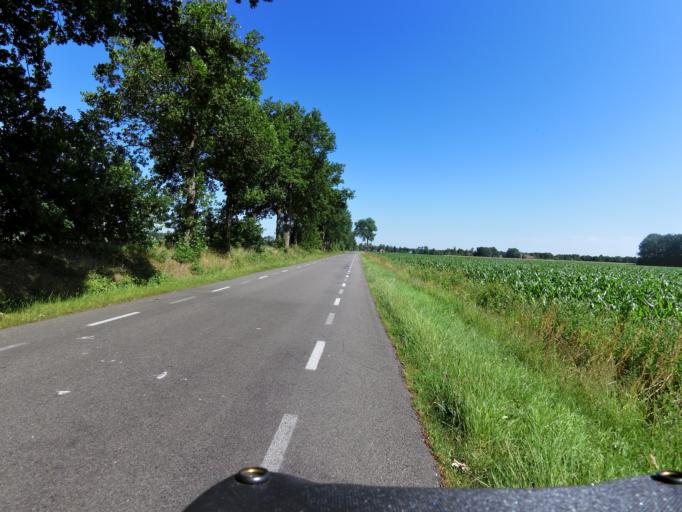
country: NL
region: Overijssel
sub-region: Gemeente Twenterand
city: Den Ham
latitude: 52.5311
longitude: 6.4456
